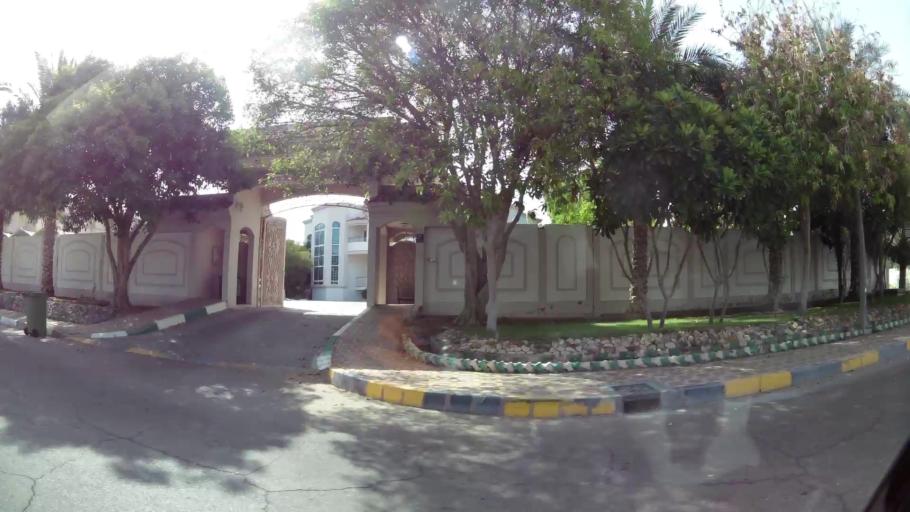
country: AE
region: Abu Dhabi
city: Al Ain
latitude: 24.2509
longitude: 55.6875
